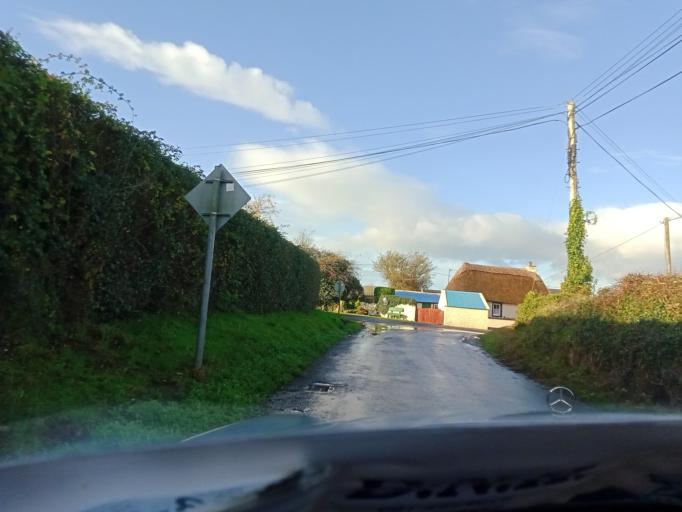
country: IE
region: Leinster
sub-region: Kilkenny
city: Mooncoin
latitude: 52.2735
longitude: -7.2323
